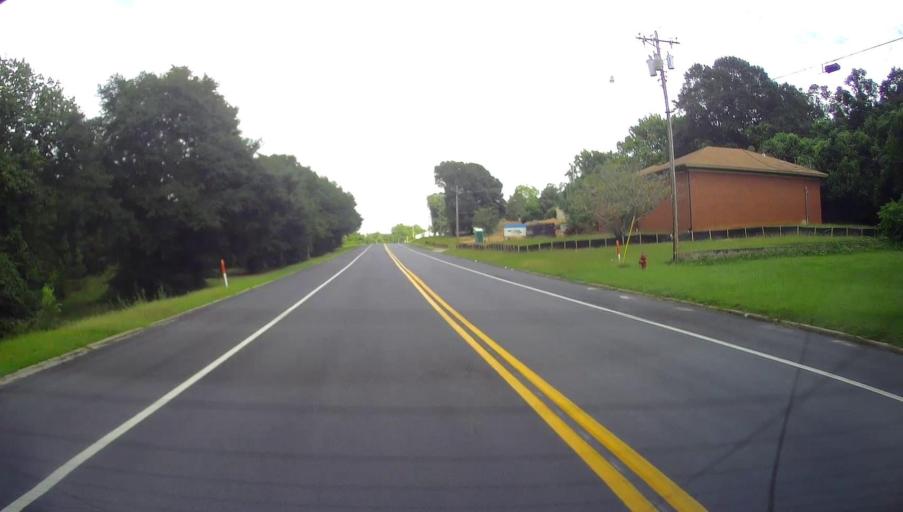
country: US
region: Georgia
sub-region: Chattahoochee County
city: Cusseta
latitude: 32.3084
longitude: -84.7866
